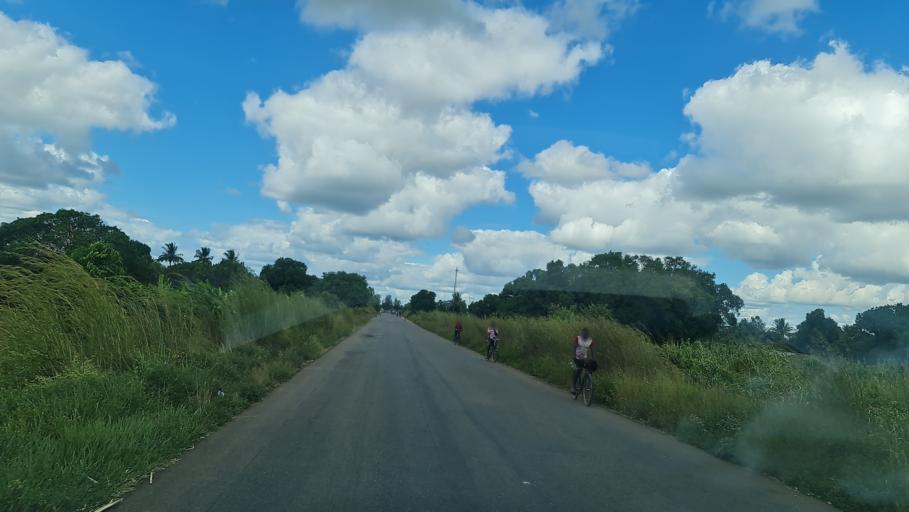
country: MZ
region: Zambezia
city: Quelimane
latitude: -17.5180
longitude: 36.2627
